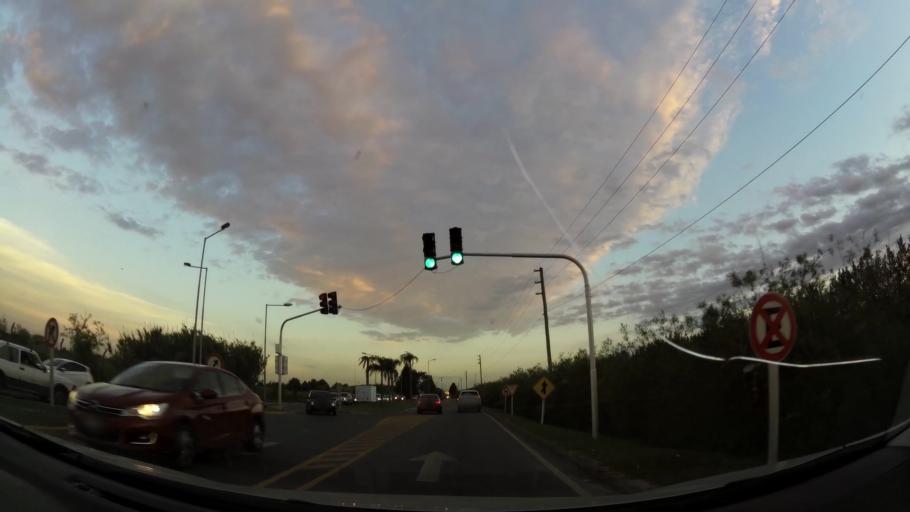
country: AR
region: Buenos Aires
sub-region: Partido de Tigre
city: Tigre
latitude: -34.4391
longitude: -58.6454
